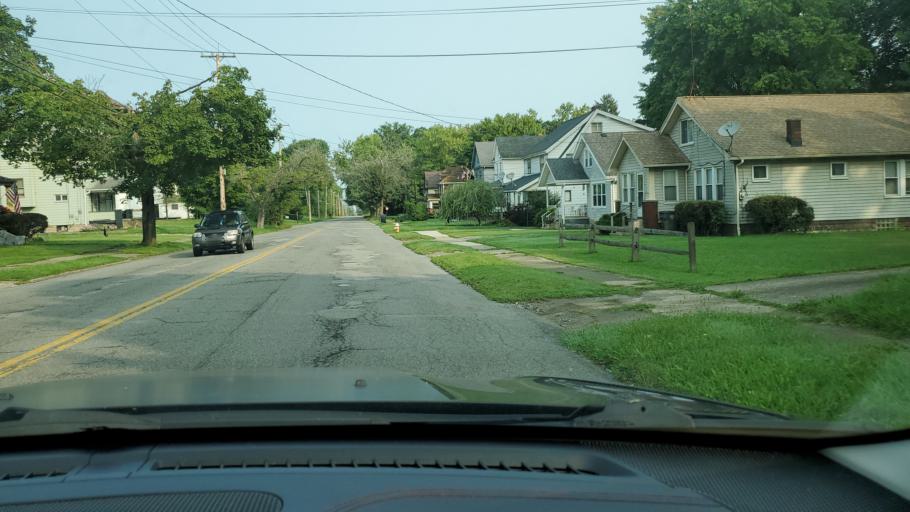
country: US
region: Ohio
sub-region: Mahoning County
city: Struthers
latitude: 41.0676
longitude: -80.6187
